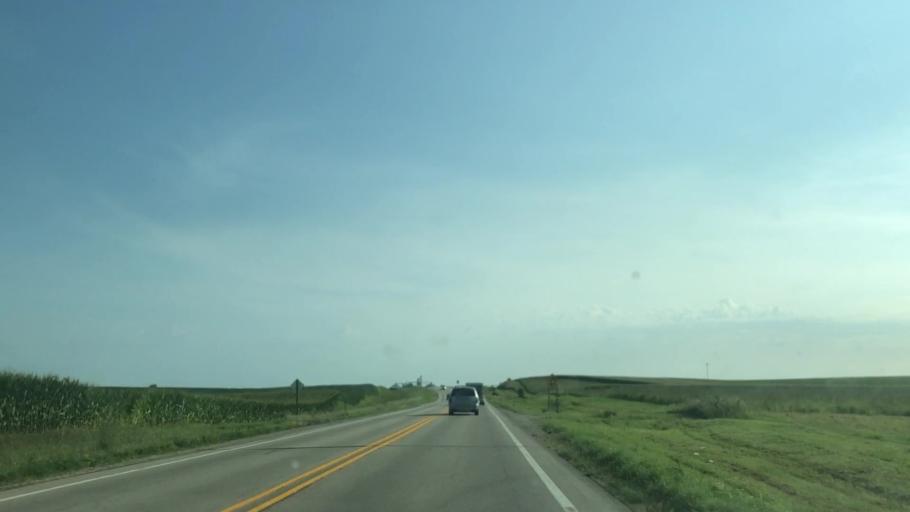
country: US
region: Iowa
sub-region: Marshall County
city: Marshalltown
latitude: 42.0192
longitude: -93.0118
